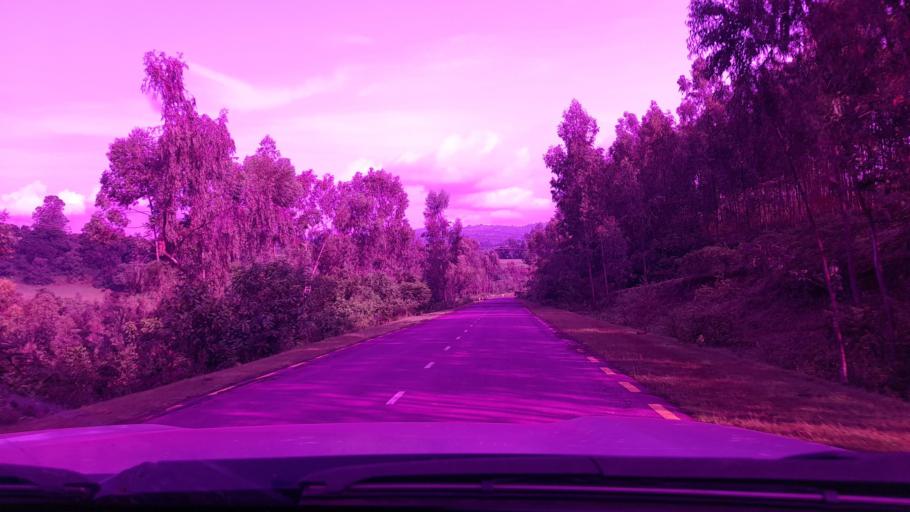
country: ET
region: Oromiya
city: Bedele
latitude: 8.2027
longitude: 36.4412
